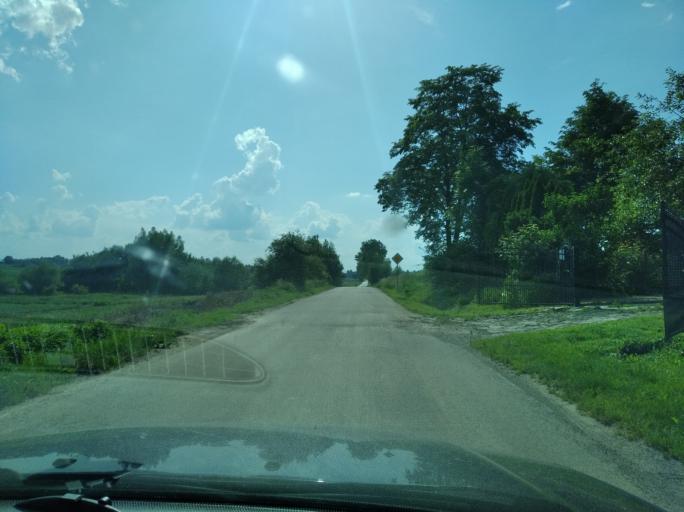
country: PL
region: Subcarpathian Voivodeship
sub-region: Powiat jaroslawski
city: Rokietnica
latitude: 49.9255
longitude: 22.7154
